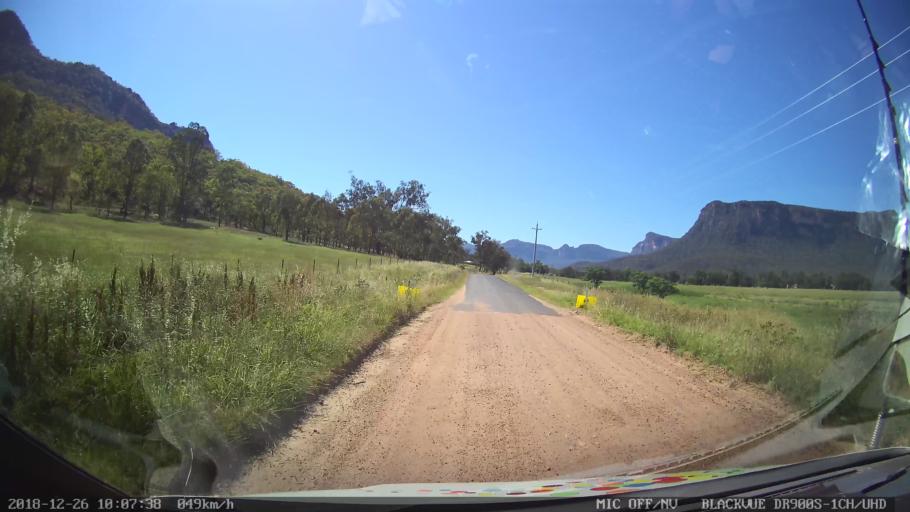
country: AU
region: New South Wales
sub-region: Mid-Western Regional
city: Kandos
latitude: -33.0918
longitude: 150.2255
